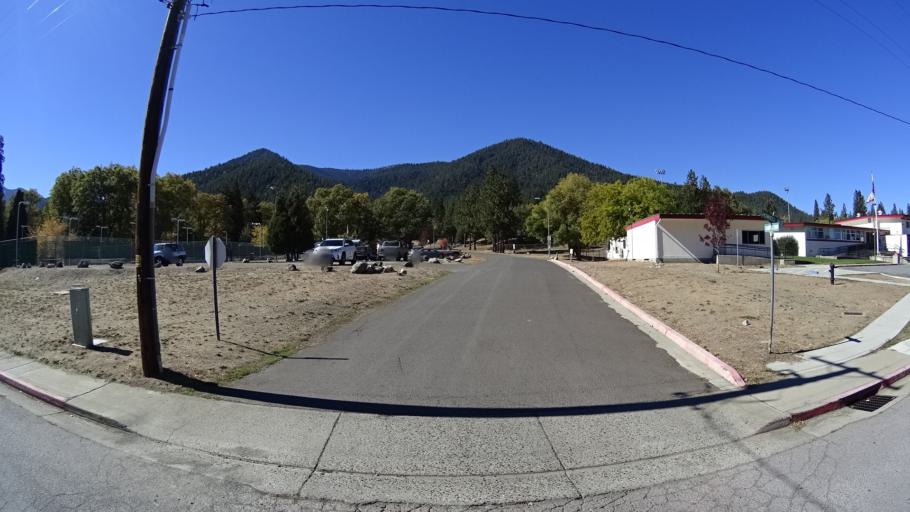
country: US
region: California
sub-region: Siskiyou County
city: Yreka
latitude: 41.4601
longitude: -122.8982
